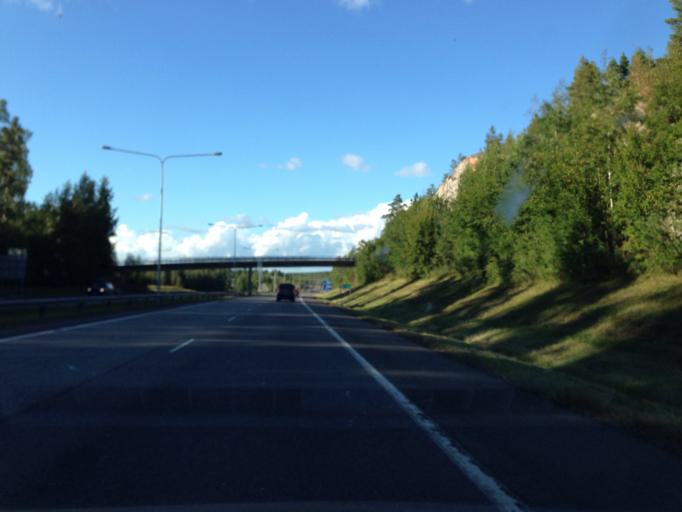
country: FI
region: Uusimaa
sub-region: Helsinki
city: Vantaa
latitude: 60.3318
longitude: 24.9991
